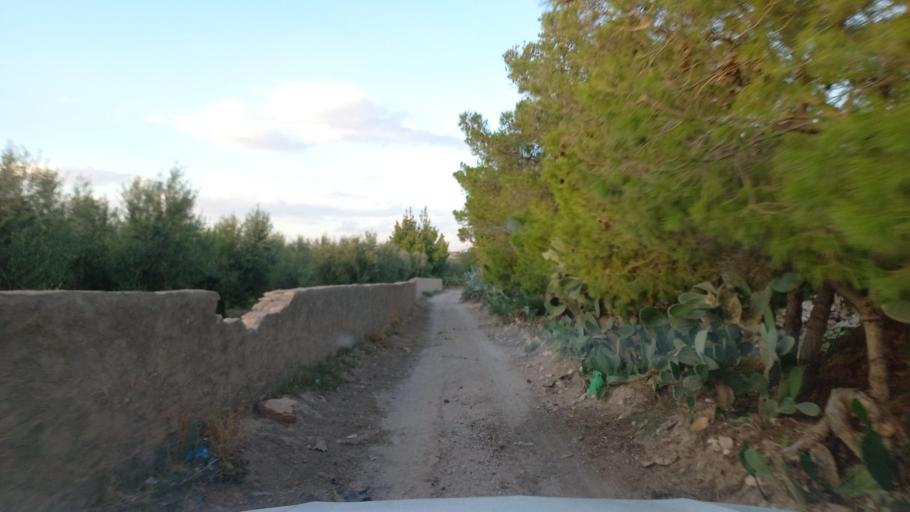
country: TN
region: Al Qasrayn
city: Sbiba
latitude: 35.3771
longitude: 9.0550
